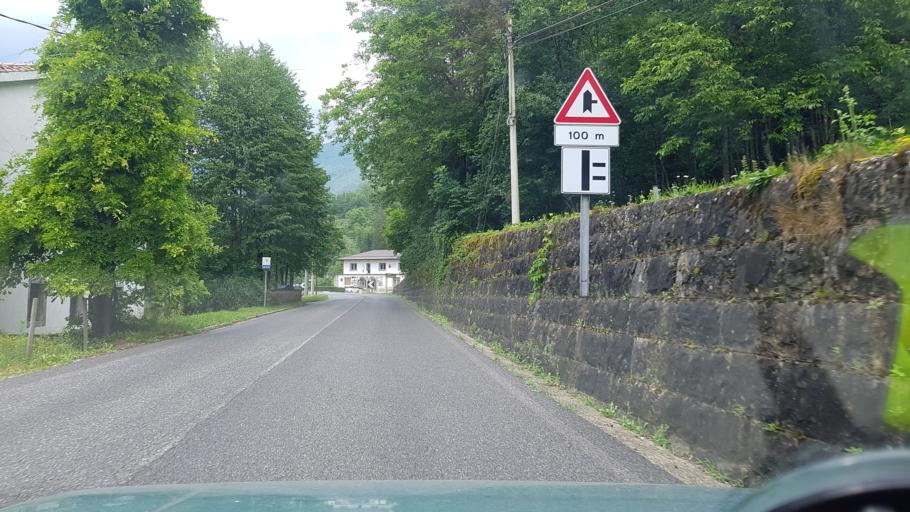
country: IT
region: Friuli Venezia Giulia
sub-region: Provincia di Udine
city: Lusevera
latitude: 46.2634
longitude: 13.2593
